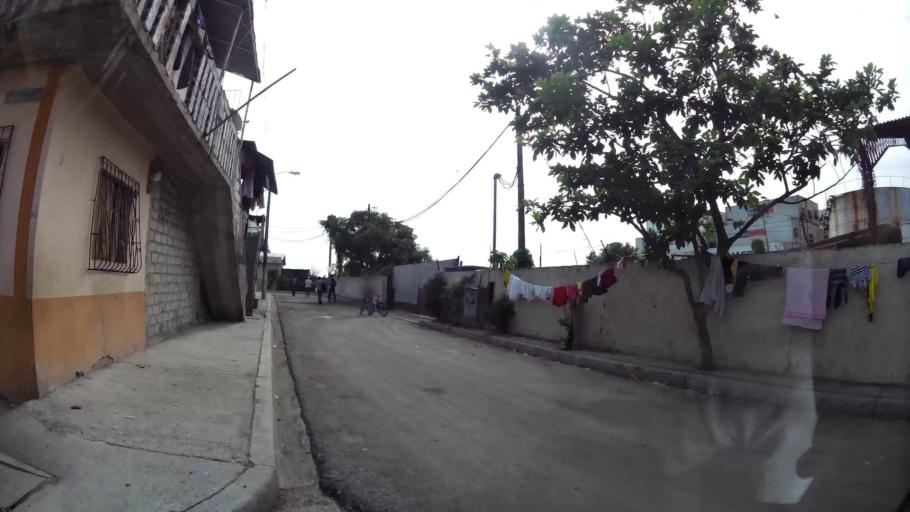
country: EC
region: Guayas
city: Guayaquil
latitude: -2.2511
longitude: -79.8760
